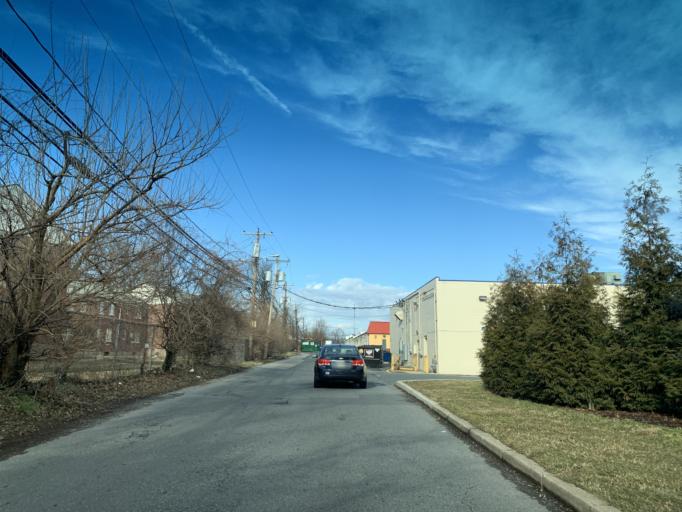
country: US
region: Delaware
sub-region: New Castle County
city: Wilmington Manor
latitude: 39.6912
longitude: -75.5822
